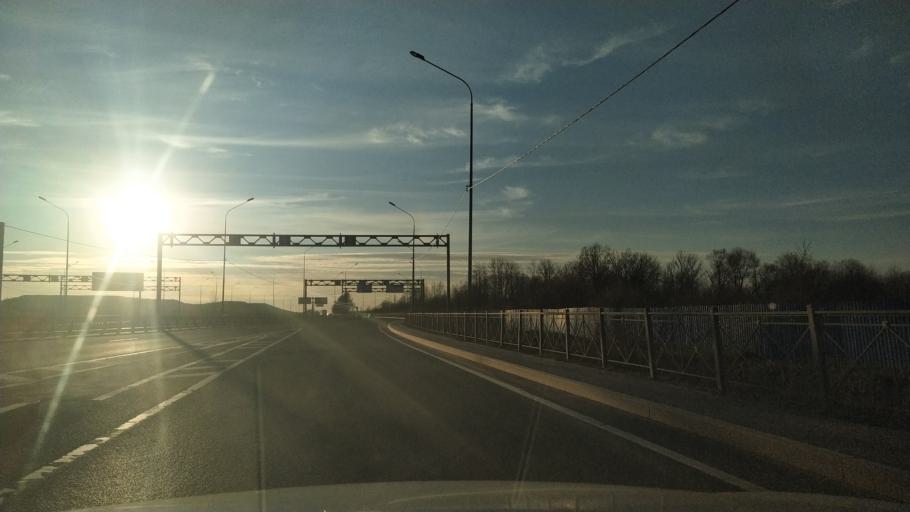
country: RU
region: St.-Petersburg
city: Aleksandrovskaya
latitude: 59.7467
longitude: 30.3041
